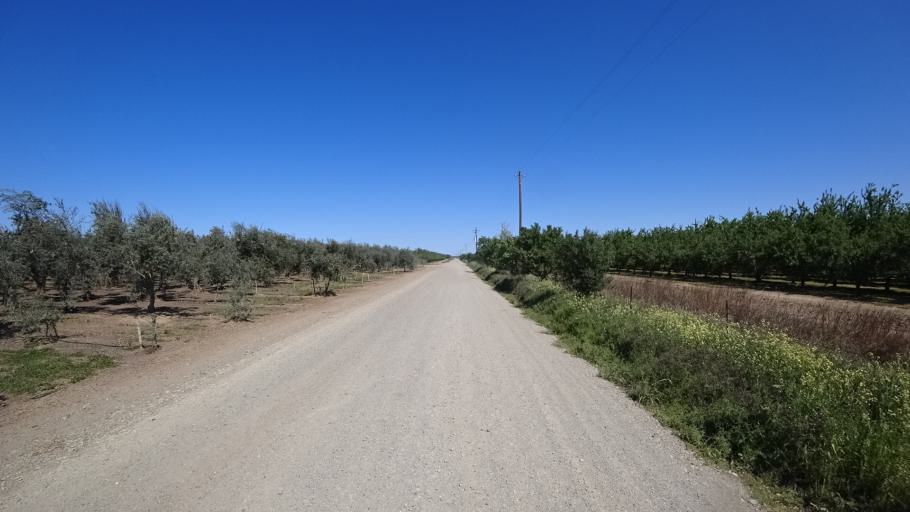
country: US
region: California
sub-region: Glenn County
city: Orland
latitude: 39.6880
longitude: -122.1592
